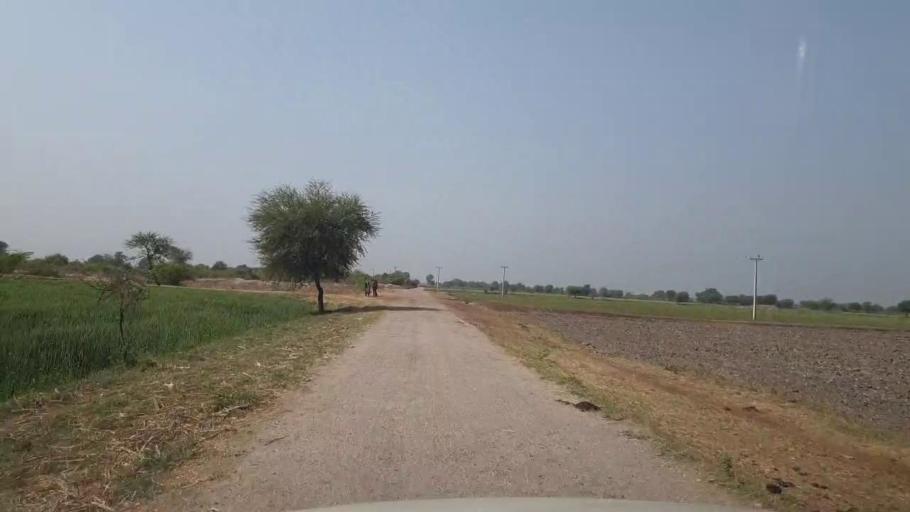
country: PK
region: Sindh
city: Chor
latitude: 25.4658
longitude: 69.6719
